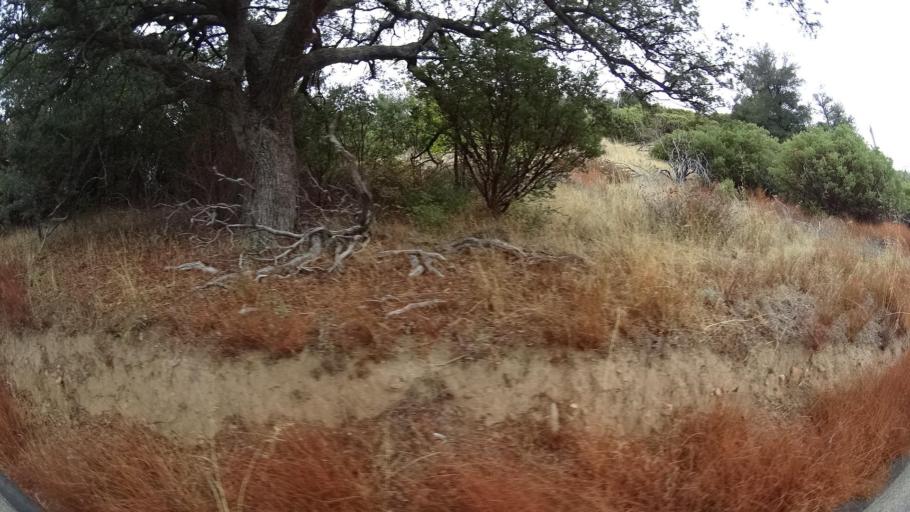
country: US
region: California
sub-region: San Diego County
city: Julian
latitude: 33.0169
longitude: -116.6331
